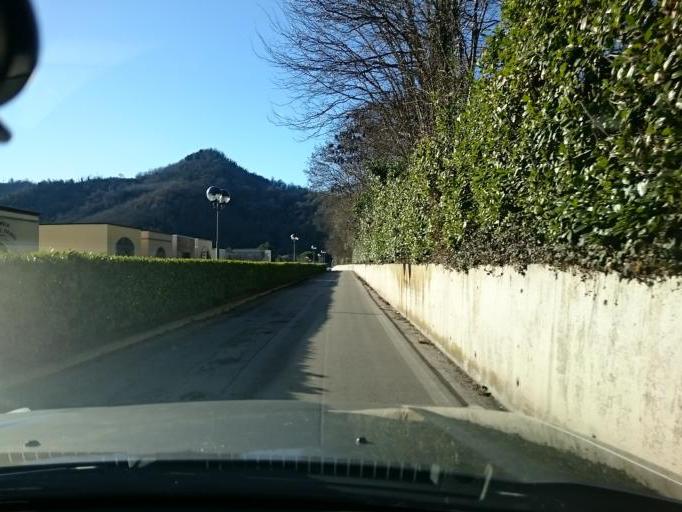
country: IT
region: Veneto
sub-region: Provincia di Padova
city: Montegrotto Terme
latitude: 45.3274
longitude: 11.7786
